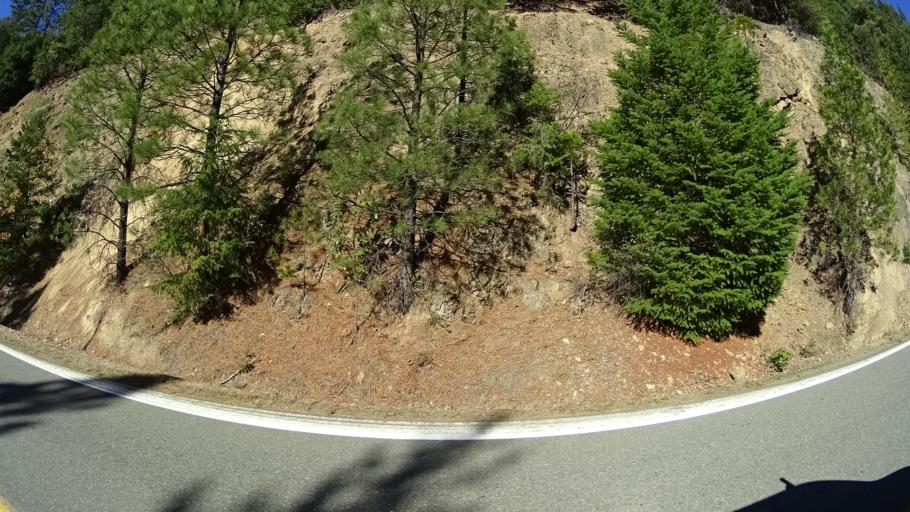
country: US
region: California
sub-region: Trinity County
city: Weaverville
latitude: 41.2128
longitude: -123.0293
